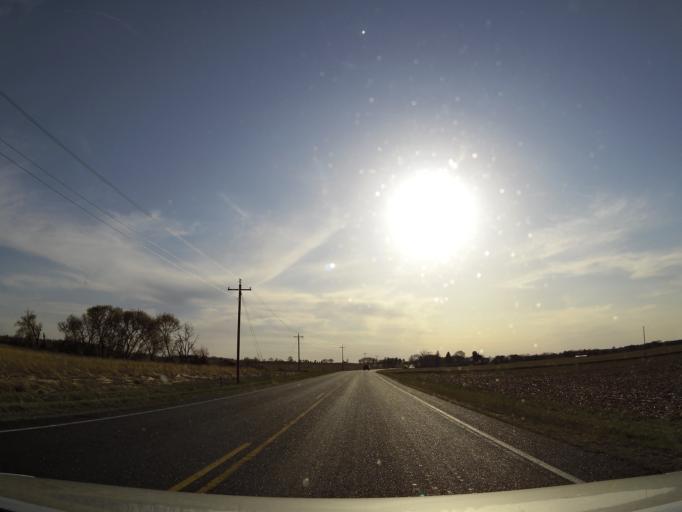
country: US
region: Wisconsin
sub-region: Pierce County
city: River Falls
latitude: 44.8248
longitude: -92.6991
